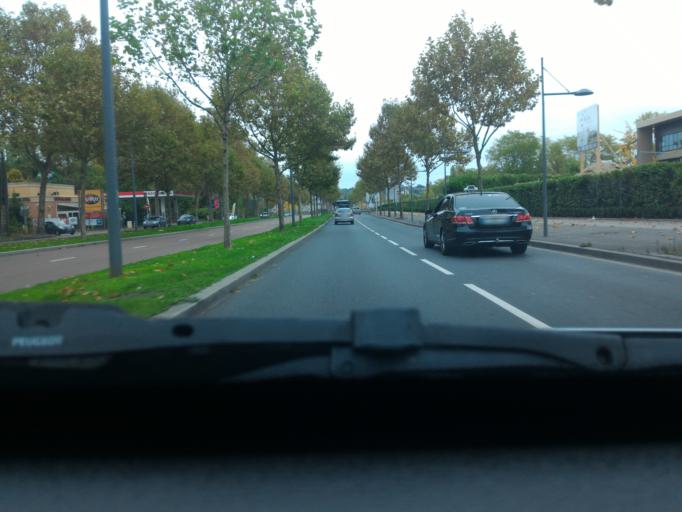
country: FR
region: Ile-de-France
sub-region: Departement du Val-de-Marne
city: Bonneuil-sur-Marne
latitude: 48.7730
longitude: 2.4967
